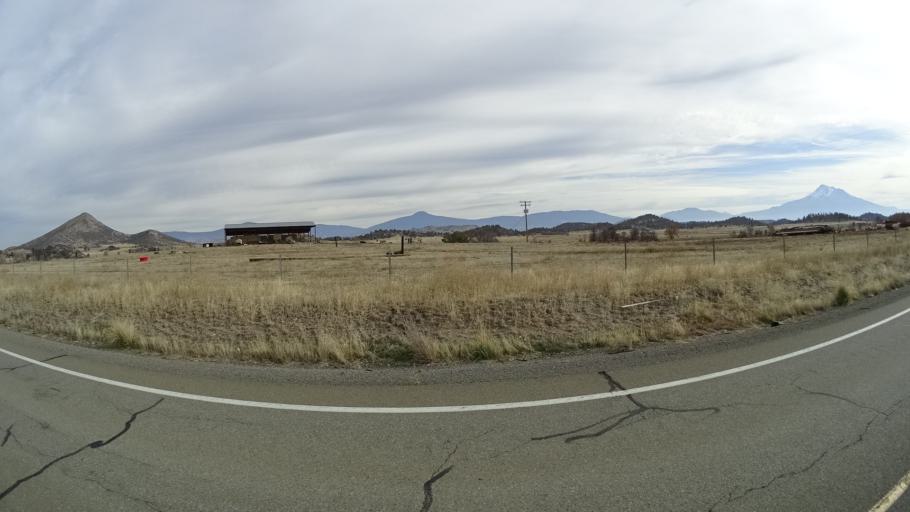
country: US
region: California
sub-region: Siskiyou County
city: Montague
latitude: 41.6957
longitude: -122.5350
